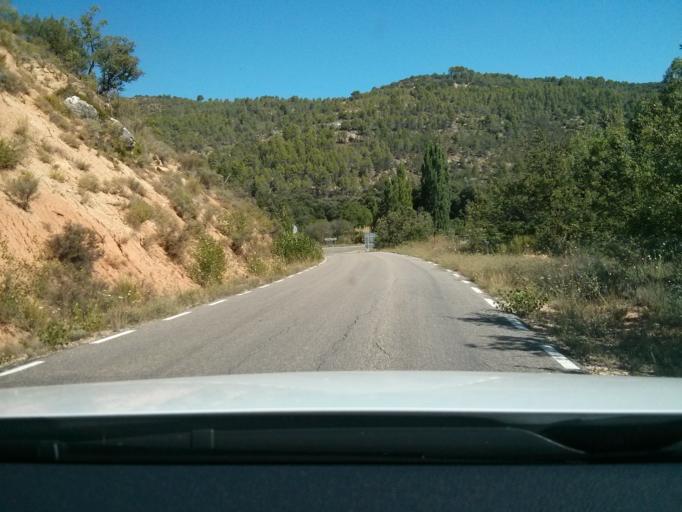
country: ES
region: Castille-La Mancha
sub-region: Provincia de Guadalajara
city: Mantiel
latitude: 40.6351
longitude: -2.6457
